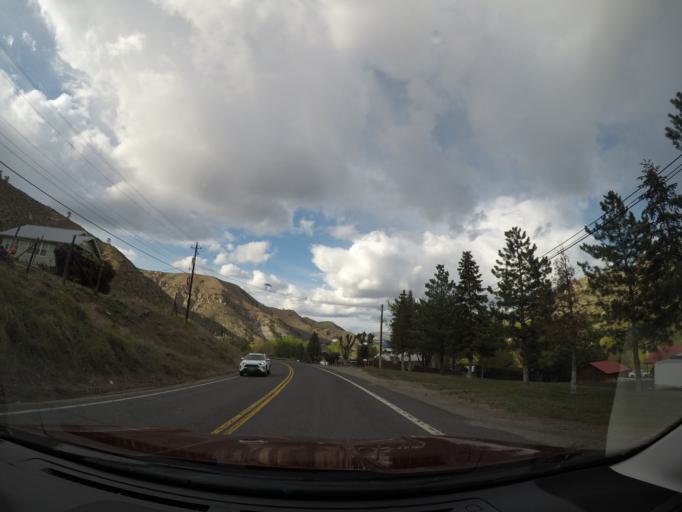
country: US
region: Washington
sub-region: Chelan County
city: South Wenatchee
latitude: 47.3672
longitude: -120.3231
